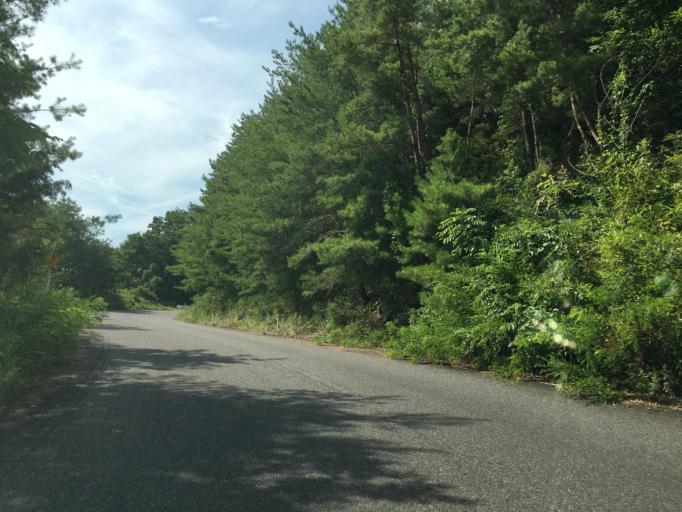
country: JP
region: Fukushima
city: Sukagawa
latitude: 37.2250
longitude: 140.4211
